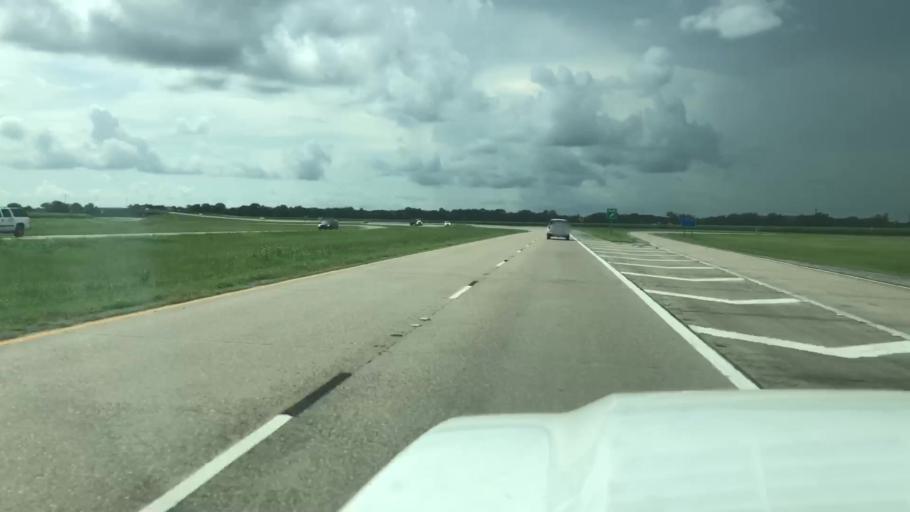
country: US
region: Louisiana
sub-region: Saint Mary Parish
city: Franklin
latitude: 29.7565
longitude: -91.4551
